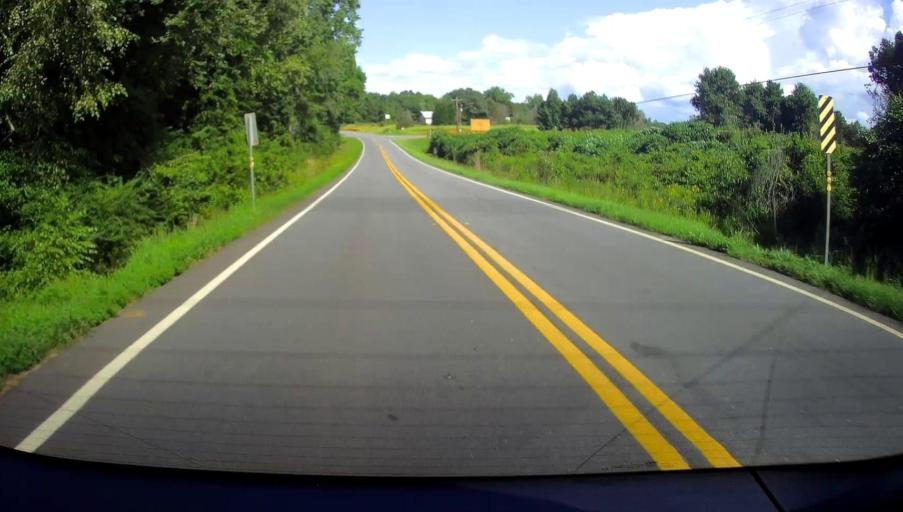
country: US
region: Georgia
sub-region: Upson County
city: Hannahs Mill
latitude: 32.8992
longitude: -84.4147
